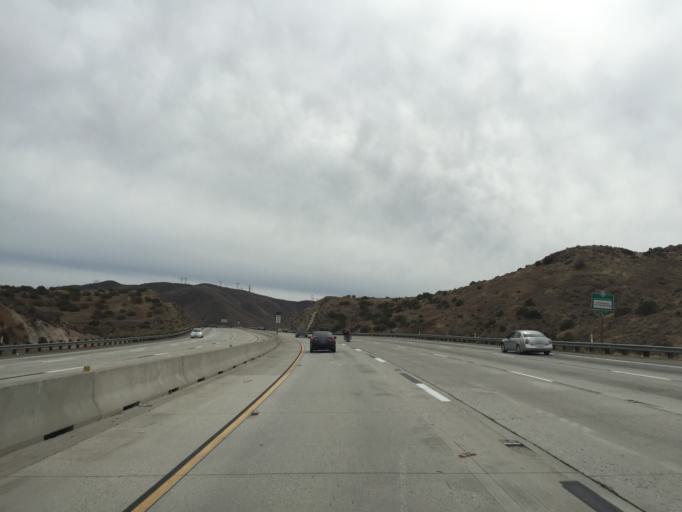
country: US
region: California
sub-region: Los Angeles County
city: Vincent
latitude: 34.5282
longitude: -118.1136
